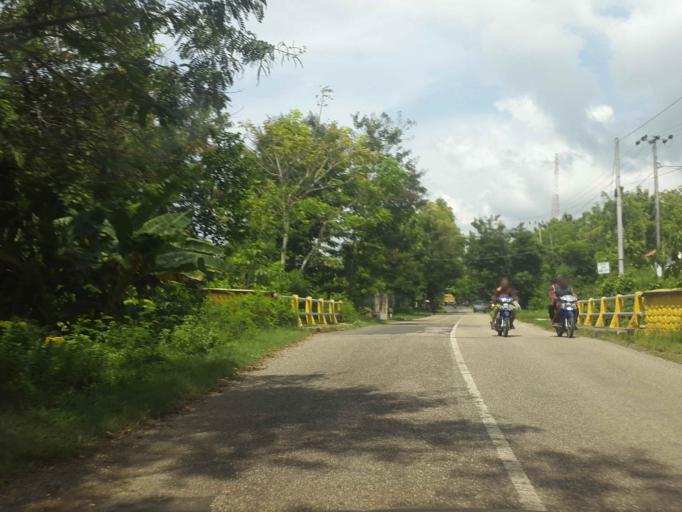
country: ID
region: East Java
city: Barru
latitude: -7.1093
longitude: 113.6869
